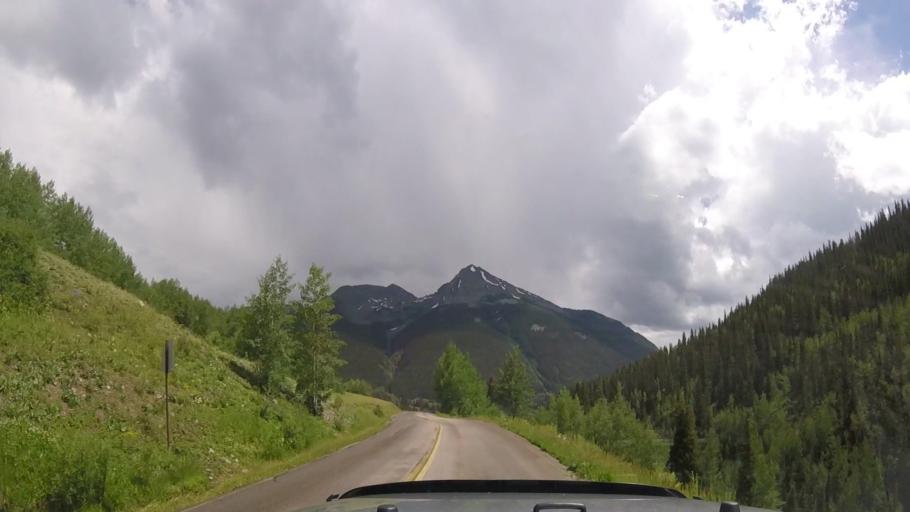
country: US
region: Colorado
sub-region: San Juan County
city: Silverton
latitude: 37.8222
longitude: -107.6644
